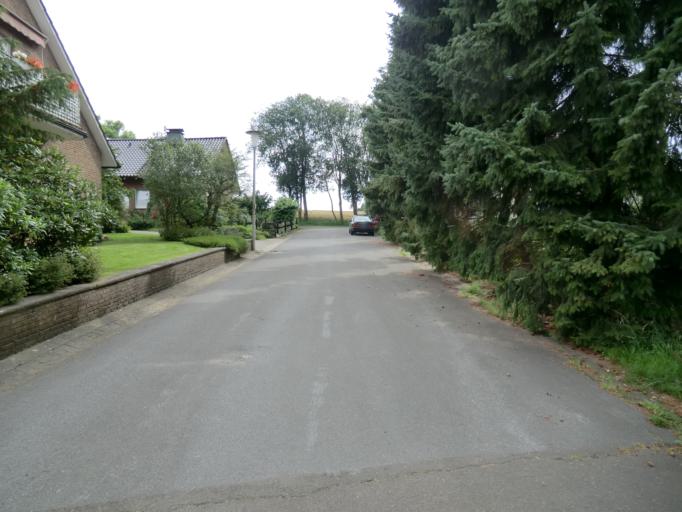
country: DE
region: North Rhine-Westphalia
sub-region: Regierungsbezirk Detmold
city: Hiddenhausen
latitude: 52.1666
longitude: 8.6079
